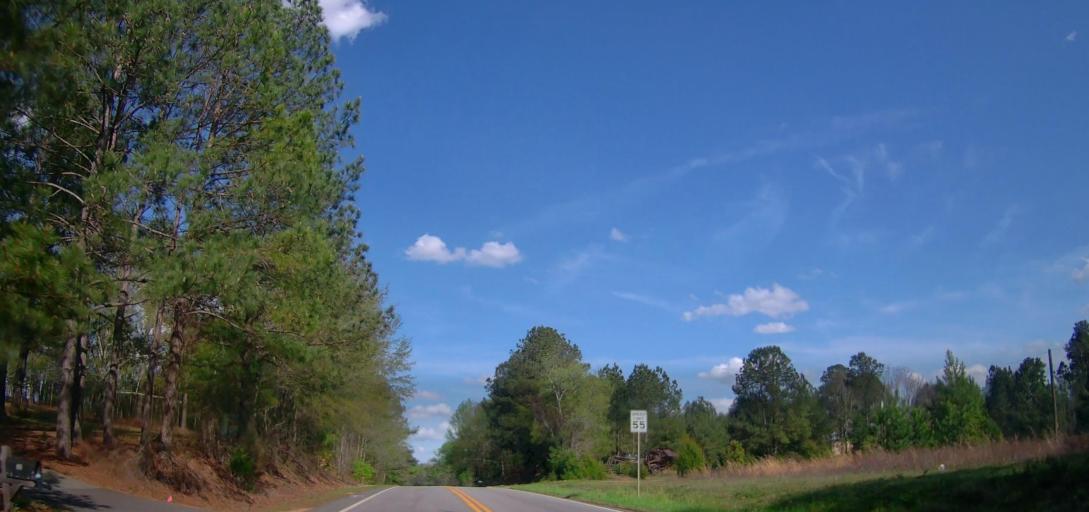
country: US
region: Georgia
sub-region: Baldwin County
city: Hardwick
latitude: 33.0802
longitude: -83.1581
